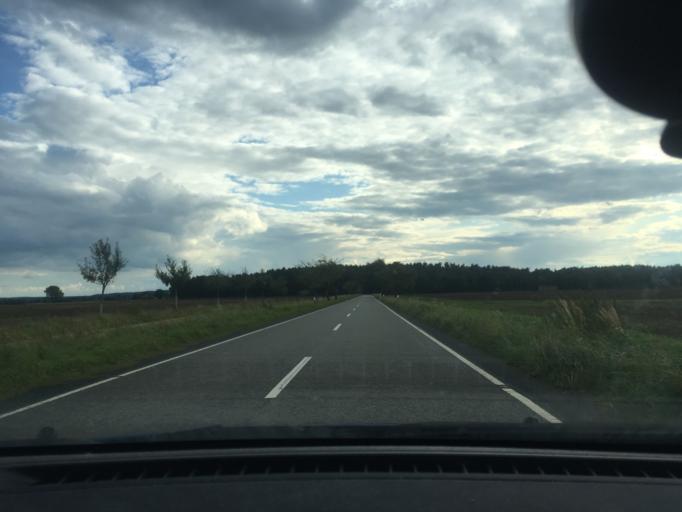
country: DE
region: Lower Saxony
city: Neu Darchau
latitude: 53.2697
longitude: 10.9236
